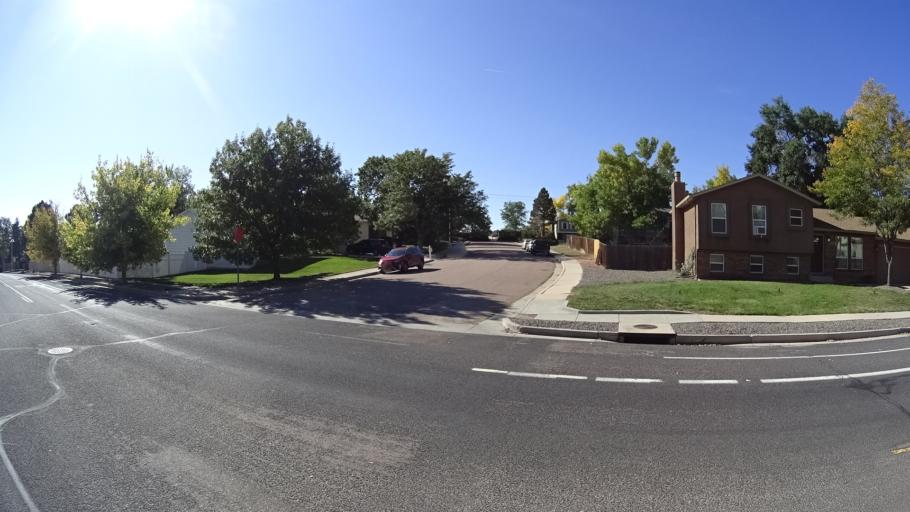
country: US
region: Colorado
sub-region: El Paso County
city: Colorado Springs
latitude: 38.9051
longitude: -104.7871
